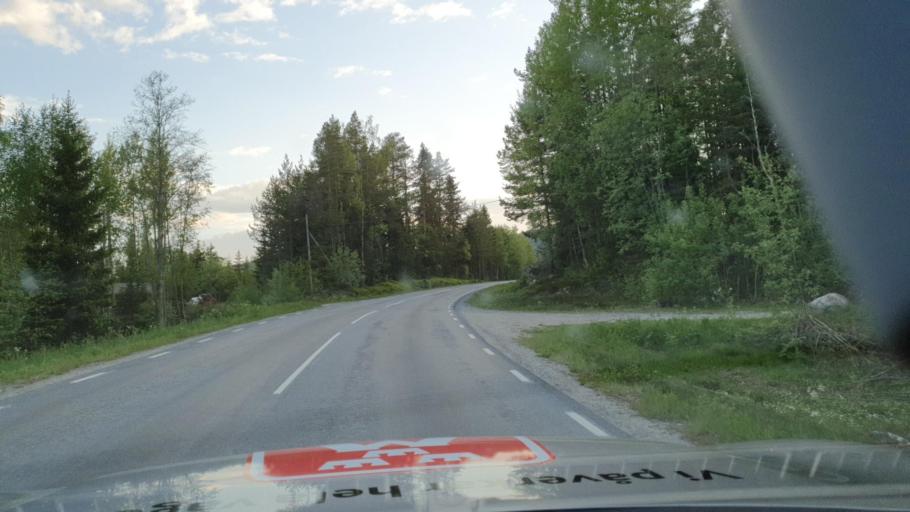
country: SE
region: Vaesternorrland
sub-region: OErnskoeldsviks Kommun
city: Ornskoldsvik
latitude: 63.2512
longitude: 18.6700
